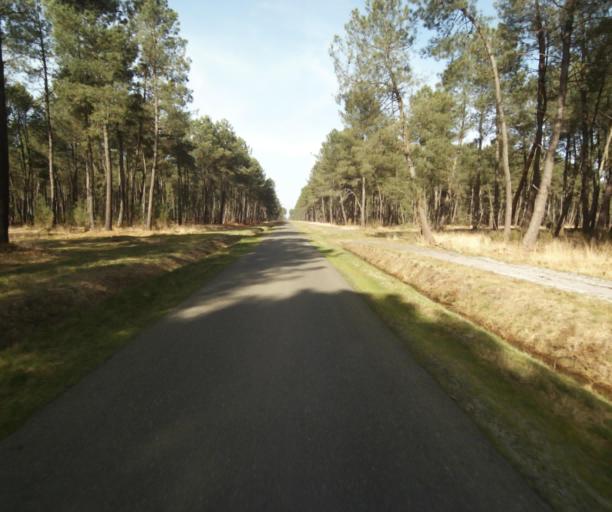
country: FR
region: Aquitaine
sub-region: Departement des Landes
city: Roquefort
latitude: 44.1883
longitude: -0.1913
